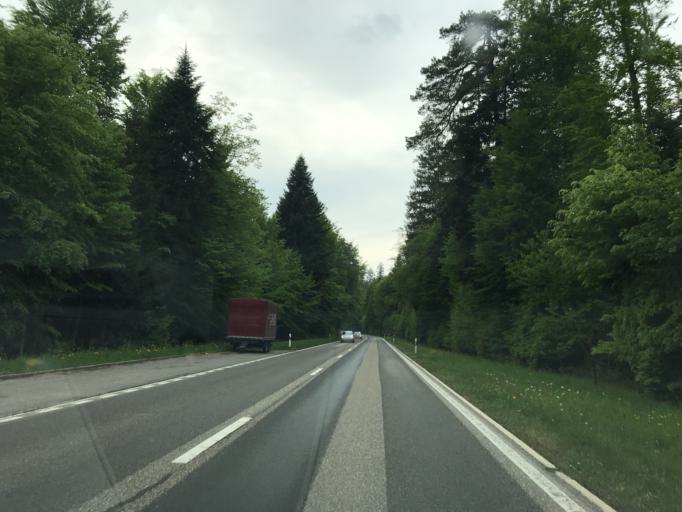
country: CH
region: Bern
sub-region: Oberaargau
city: Aarwangen
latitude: 47.2484
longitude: 7.7511
